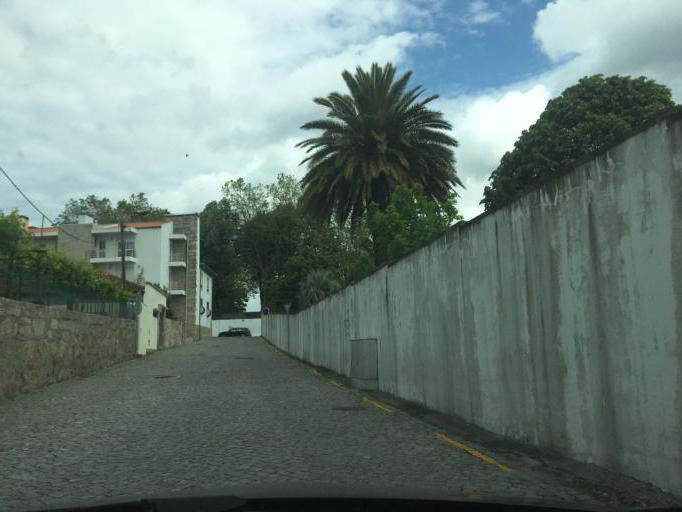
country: PT
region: Porto
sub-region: Maia
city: Anta
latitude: 41.2642
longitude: -8.6124
